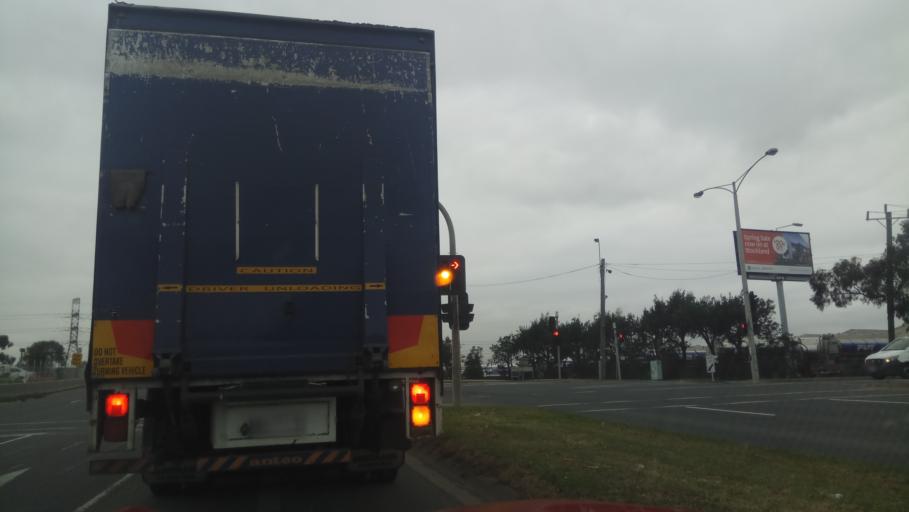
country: AU
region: Victoria
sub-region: Brimbank
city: Brooklyn
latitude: -37.8276
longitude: 144.8289
